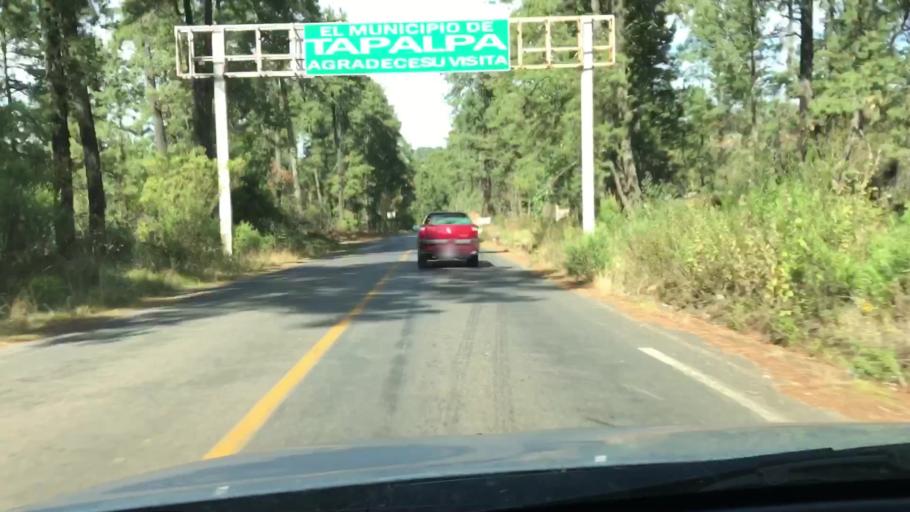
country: MX
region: Jalisco
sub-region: Amacueca
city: Tepec
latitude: 20.0846
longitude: -103.7157
